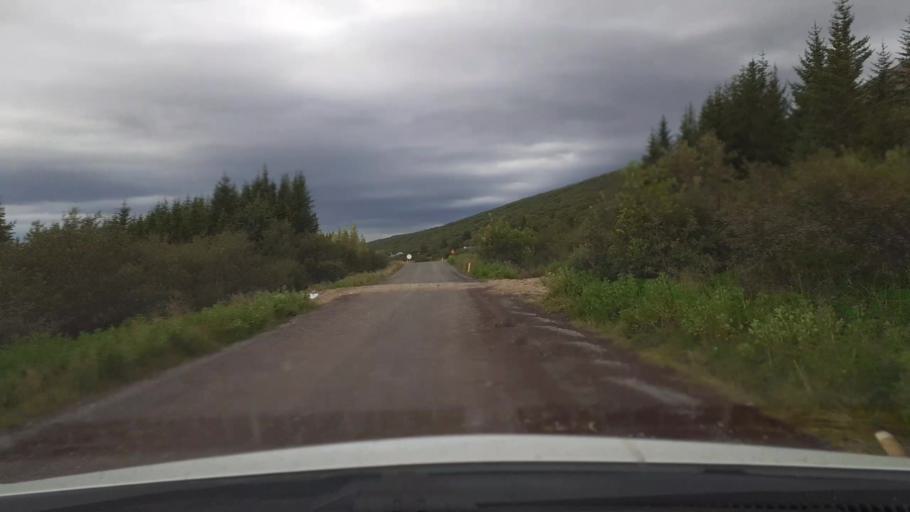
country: IS
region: West
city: Borgarnes
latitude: 64.5396
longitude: -21.5362
